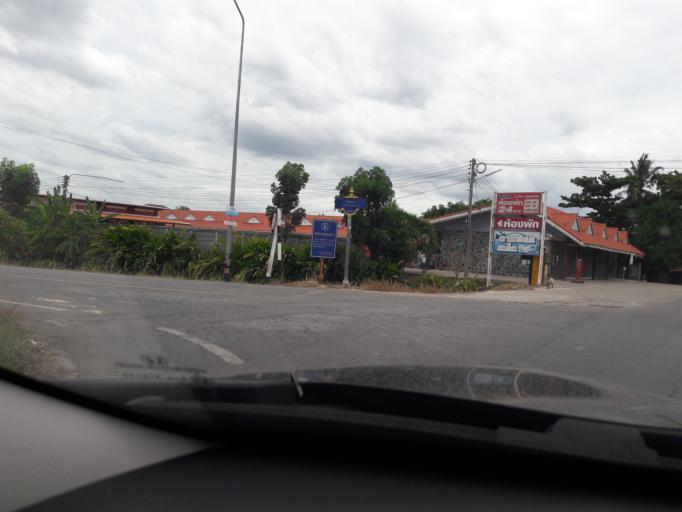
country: TH
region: Ratchaburi
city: Damnoen Saduak
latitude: 13.5921
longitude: 99.9462
